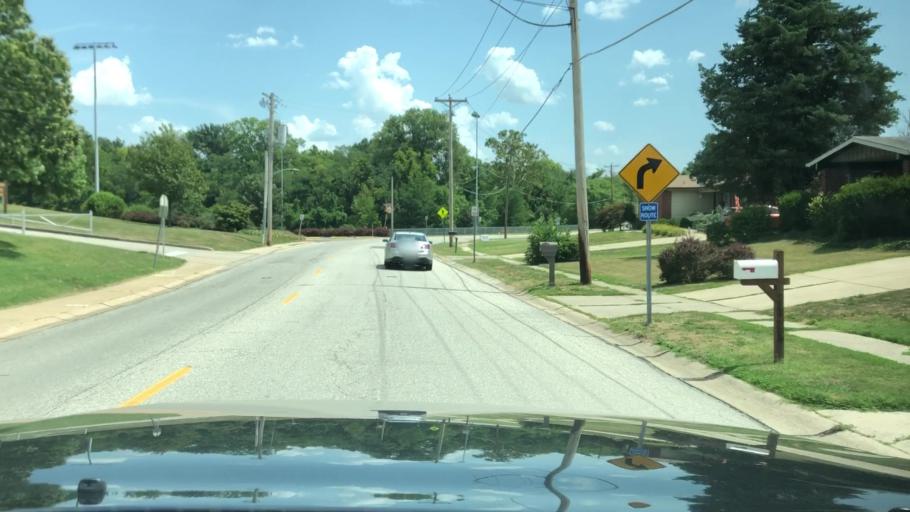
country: US
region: Missouri
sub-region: Saint Charles County
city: Saint Charles
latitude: 38.7981
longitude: -90.5268
